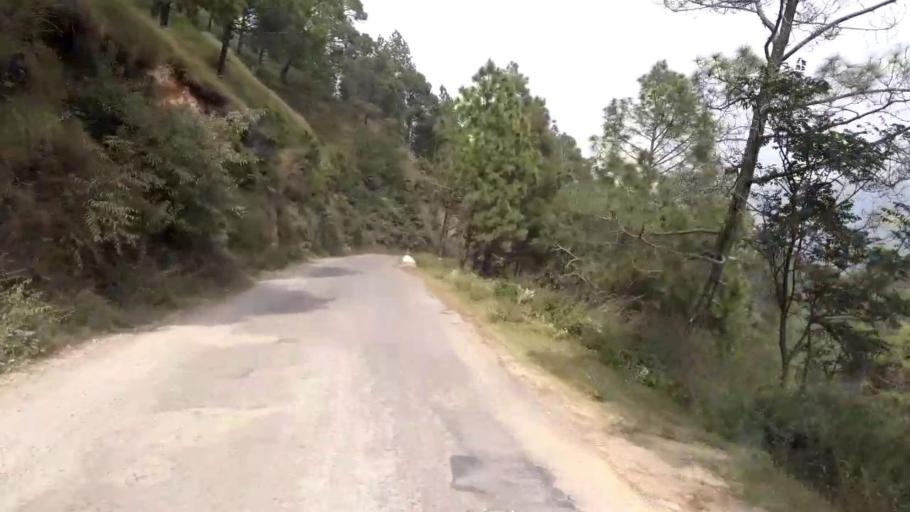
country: IN
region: Himachal Pradesh
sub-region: Shimla
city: Shimla
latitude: 31.0510
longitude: 77.1538
